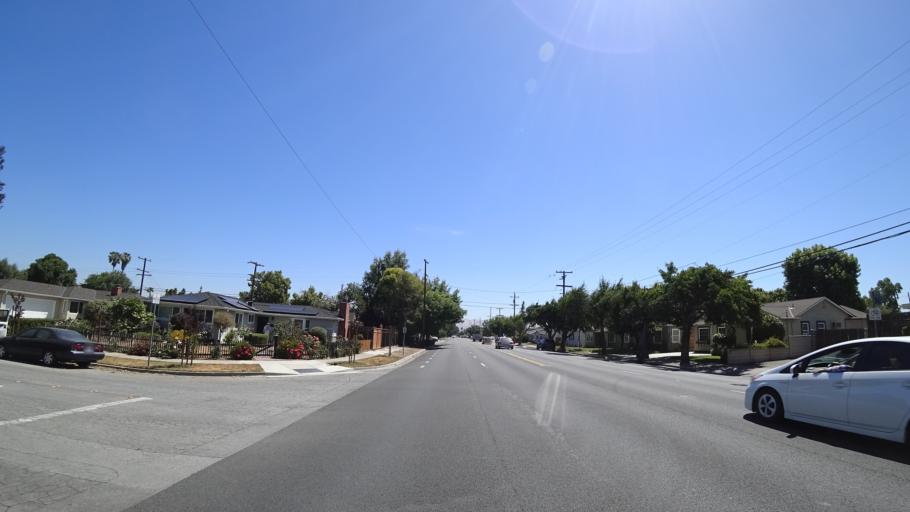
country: US
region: California
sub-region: Santa Clara County
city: Buena Vista
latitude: 37.2853
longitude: -121.9006
